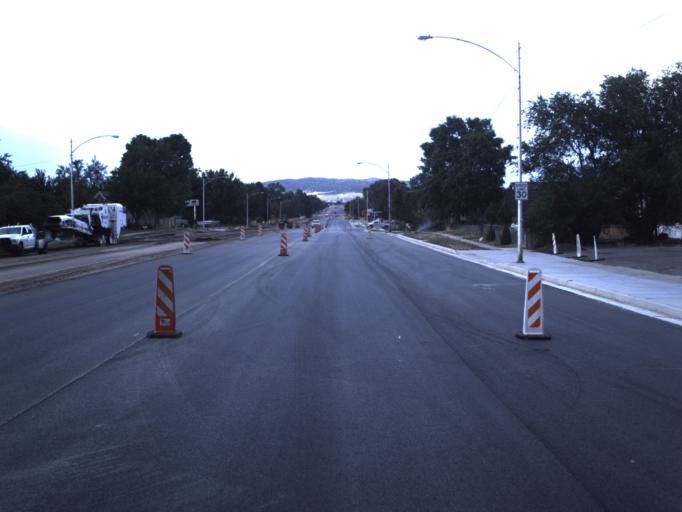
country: US
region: Utah
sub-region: Millard County
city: Fillmore
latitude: 38.9712
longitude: -112.3236
